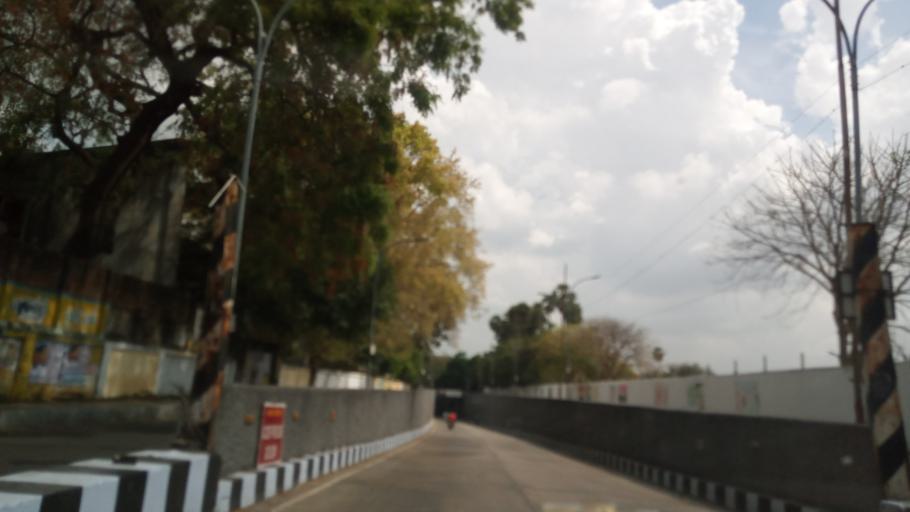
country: IN
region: Tamil Nadu
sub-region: Kancheepuram
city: Saint Thomas Mount
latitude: 12.9834
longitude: 80.1766
